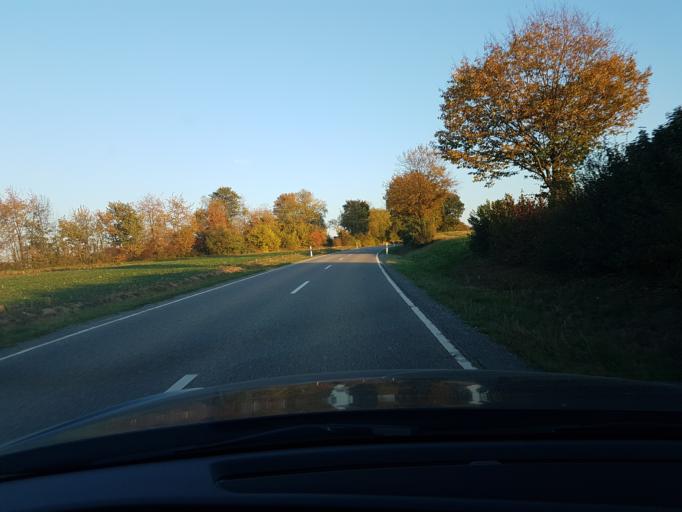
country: DE
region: Baden-Wuerttemberg
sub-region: Regierungsbezirk Stuttgart
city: Bonnigheim
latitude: 49.0596
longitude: 9.1120
